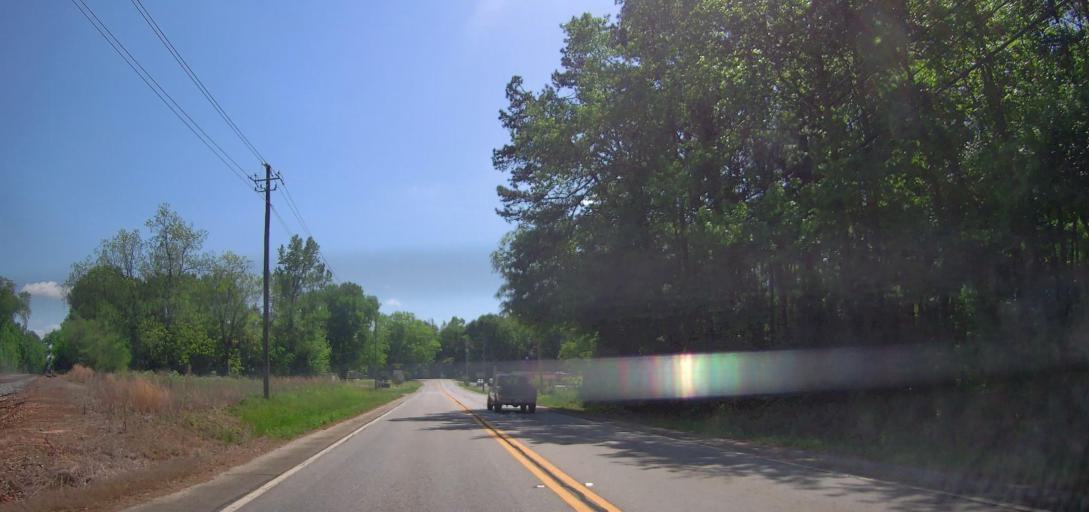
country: US
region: Georgia
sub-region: Putnam County
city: Eatonton
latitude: 33.3388
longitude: -83.3929
